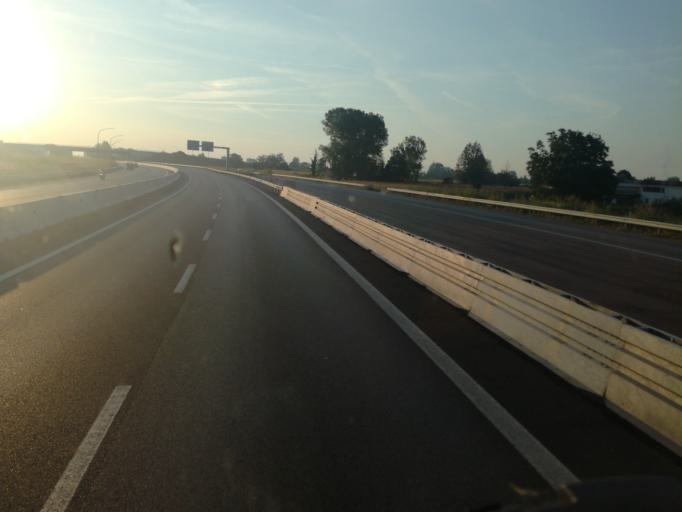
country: IT
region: Lombardy
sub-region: Provincia di Cremona
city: Spino d'Adda
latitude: 45.3913
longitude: 9.4875
